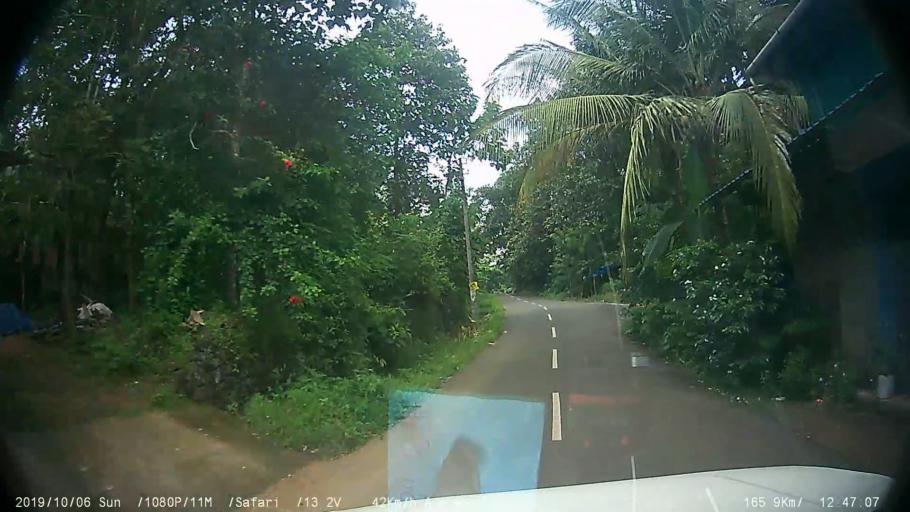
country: IN
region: Kerala
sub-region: Kottayam
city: Palackattumala
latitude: 9.7728
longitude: 76.6032
